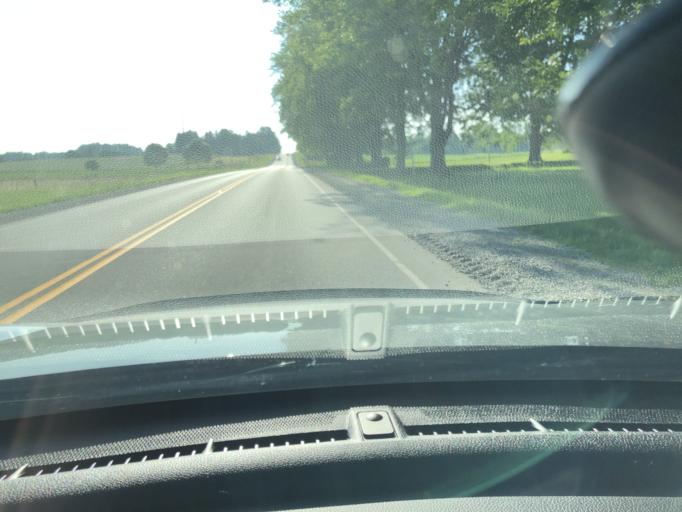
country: CA
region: Ontario
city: Stratford
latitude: 43.4246
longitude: -80.8078
